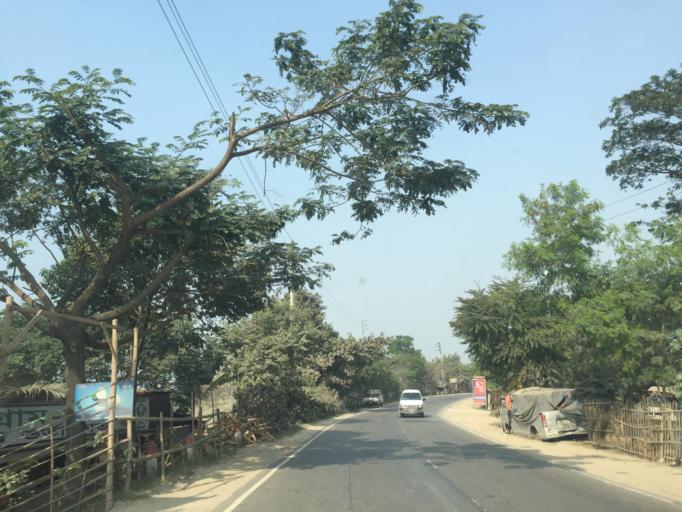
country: BD
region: Dhaka
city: Tungi
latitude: 23.8211
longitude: 90.3413
